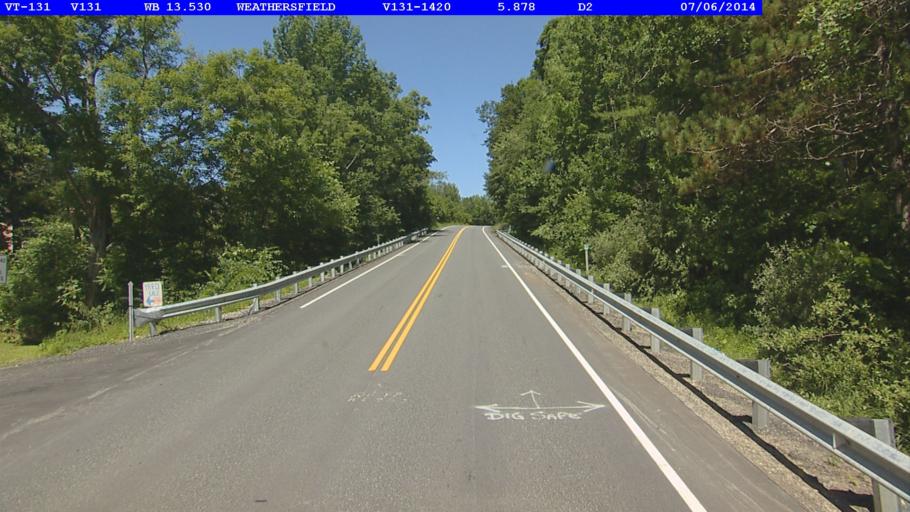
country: US
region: Vermont
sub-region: Windsor County
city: Windsor
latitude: 43.4130
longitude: -72.4556
